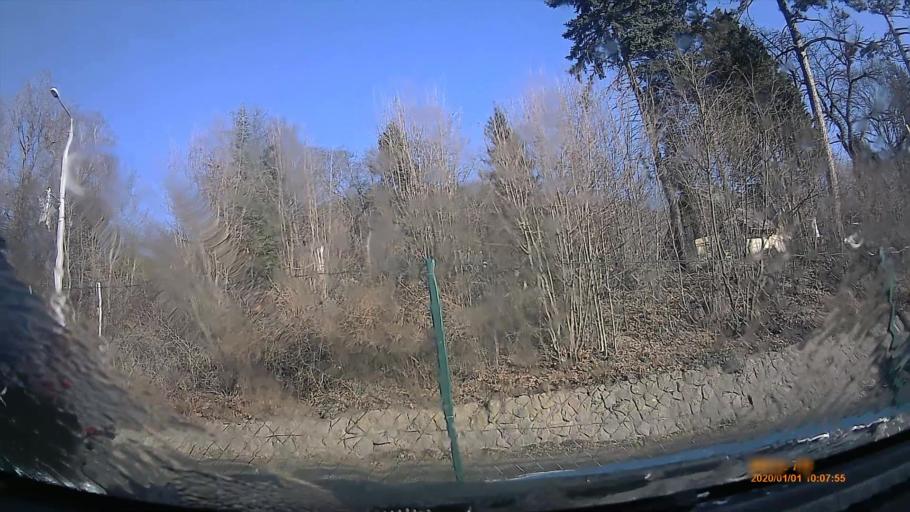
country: HU
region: Heves
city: Parad
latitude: 47.9250
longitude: 20.0610
